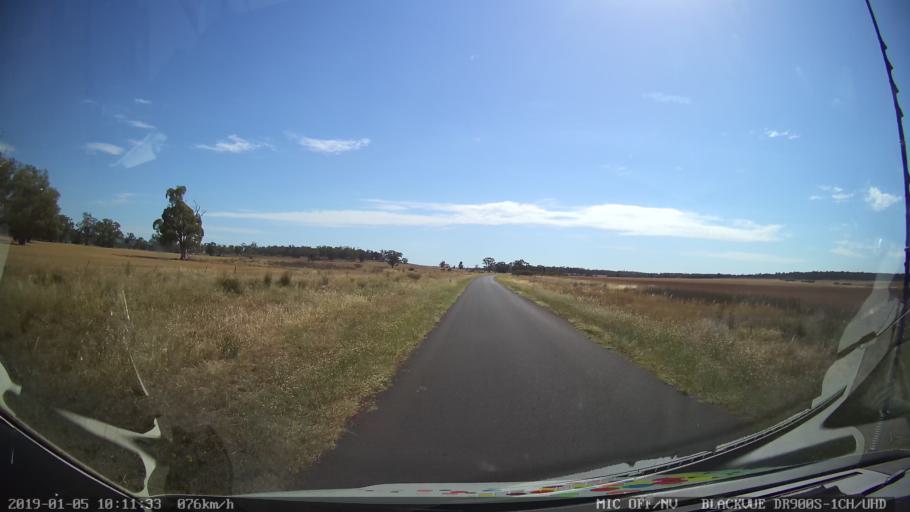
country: AU
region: New South Wales
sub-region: Gilgandra
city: Gilgandra
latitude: -31.6127
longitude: 148.9025
